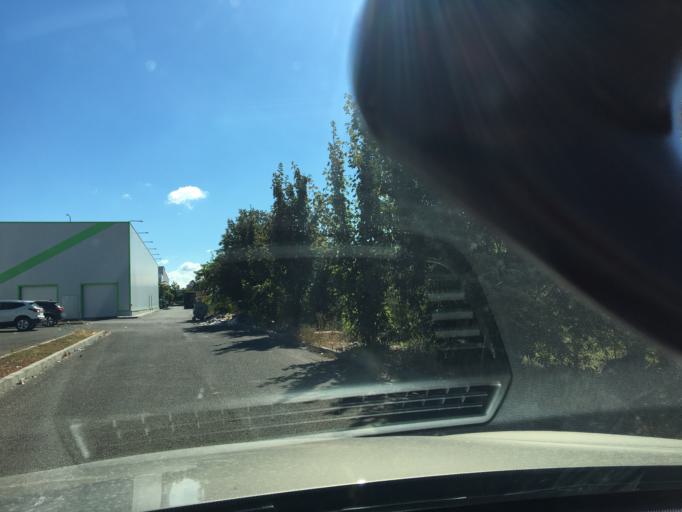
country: BG
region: Burgas
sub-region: Obshtina Burgas
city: Burgas
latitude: 42.5139
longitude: 27.4498
